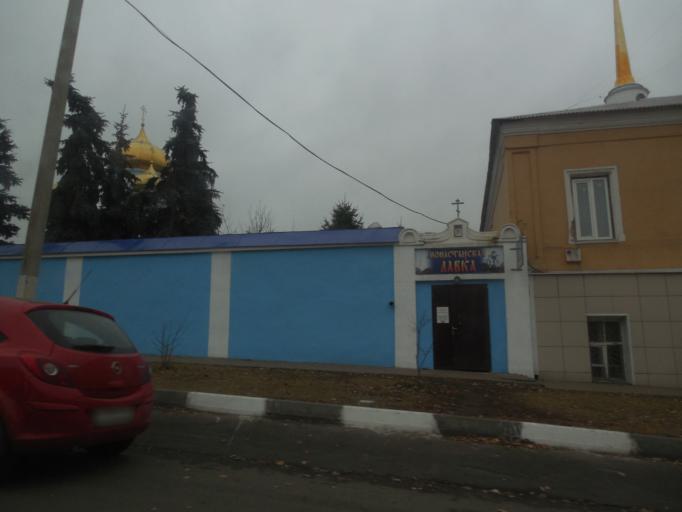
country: RU
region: Lipetsk
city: Zadonsk
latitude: 52.3931
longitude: 38.9181
